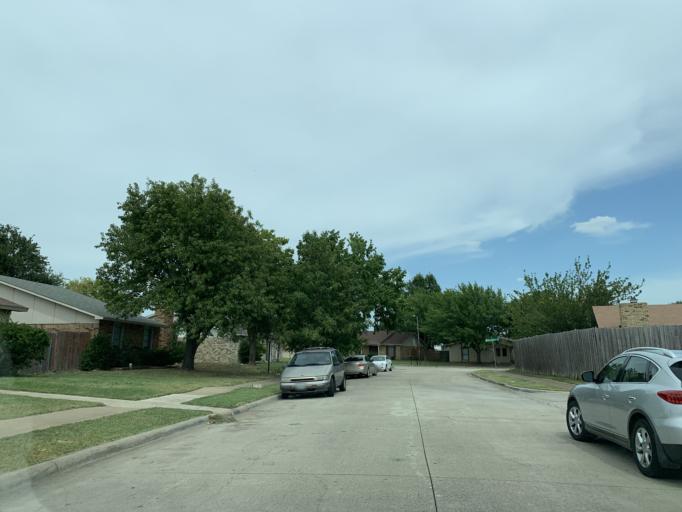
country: US
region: Texas
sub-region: Dallas County
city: Cedar Hill
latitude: 32.6516
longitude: -97.0326
